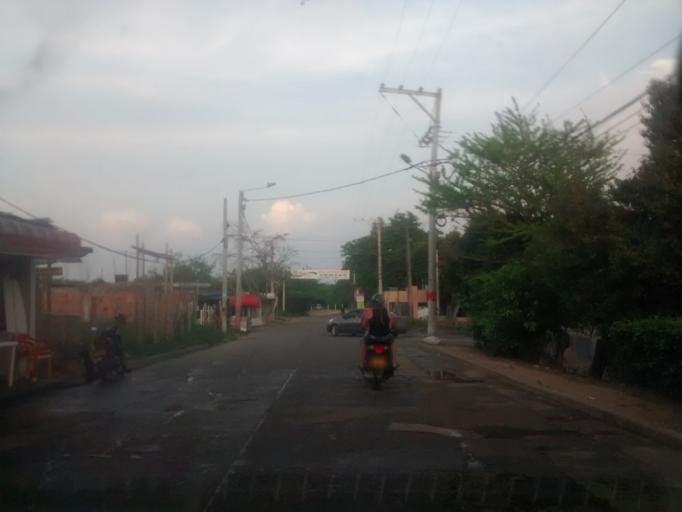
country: CO
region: Cundinamarca
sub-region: Girardot
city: Girardot City
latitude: 4.3217
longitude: -74.7861
